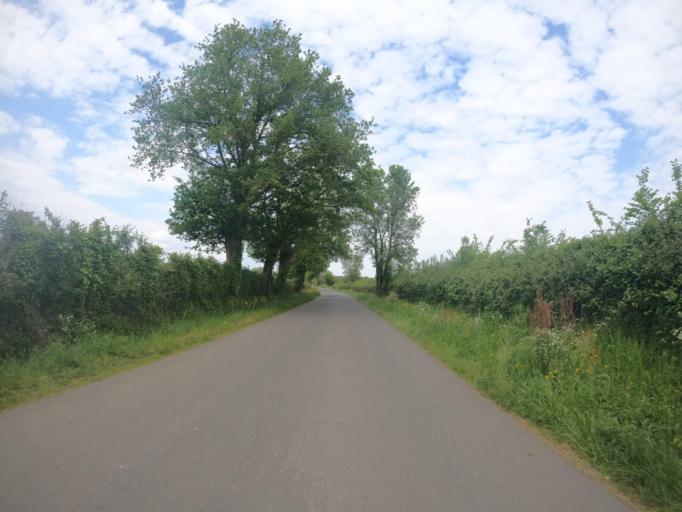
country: FR
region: Poitou-Charentes
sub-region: Departement des Deux-Sevres
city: Saint-Varent
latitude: 46.8756
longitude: -0.2961
